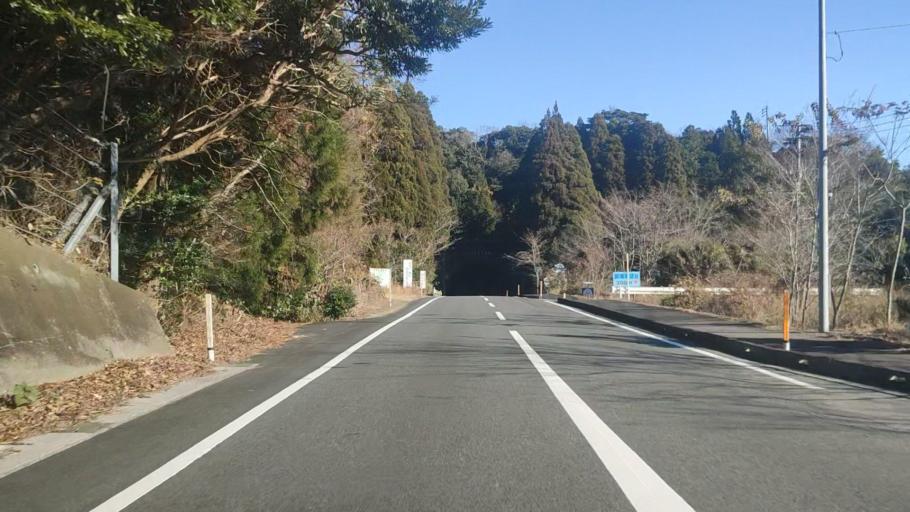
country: JP
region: Miyazaki
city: Nobeoka
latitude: 32.6970
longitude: 131.8129
